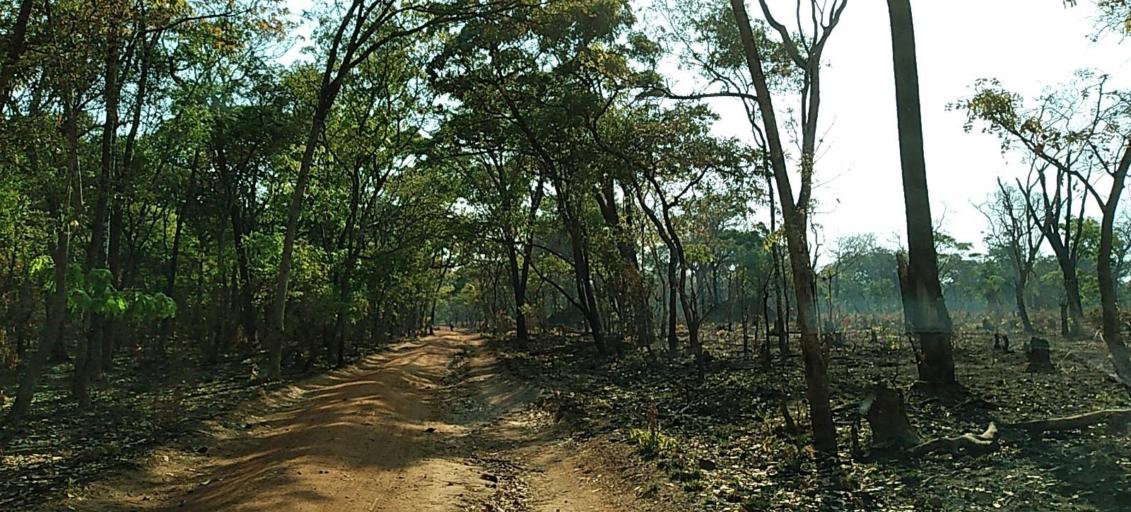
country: ZM
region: Copperbelt
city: Kalulushi
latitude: -13.0066
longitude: 27.7405
